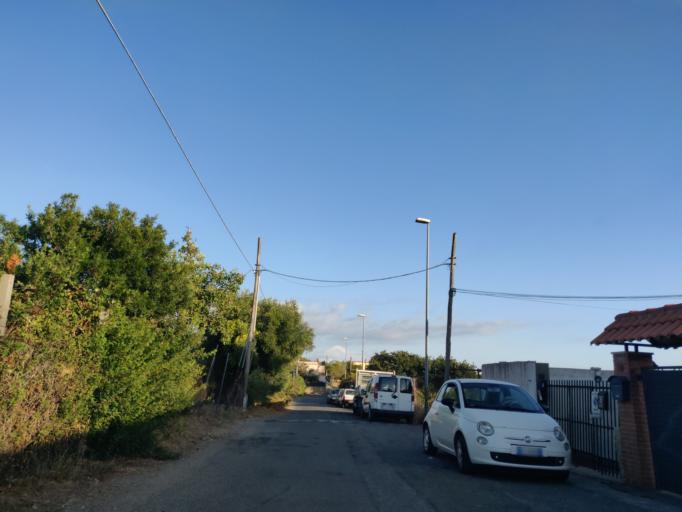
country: IT
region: Latium
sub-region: Citta metropolitana di Roma Capitale
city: Civitavecchia
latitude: 42.0916
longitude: 11.8139
